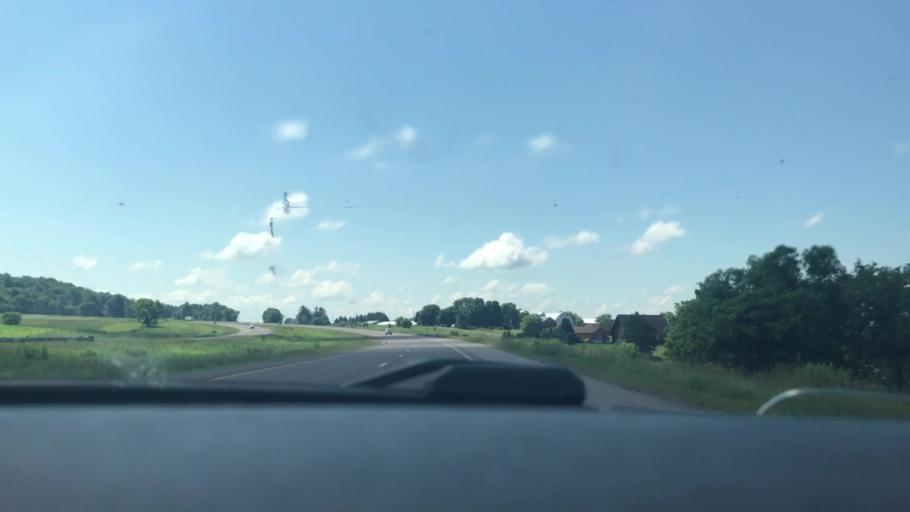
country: US
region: Wisconsin
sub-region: Chippewa County
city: Bloomer
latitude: 45.0522
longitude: -91.4657
